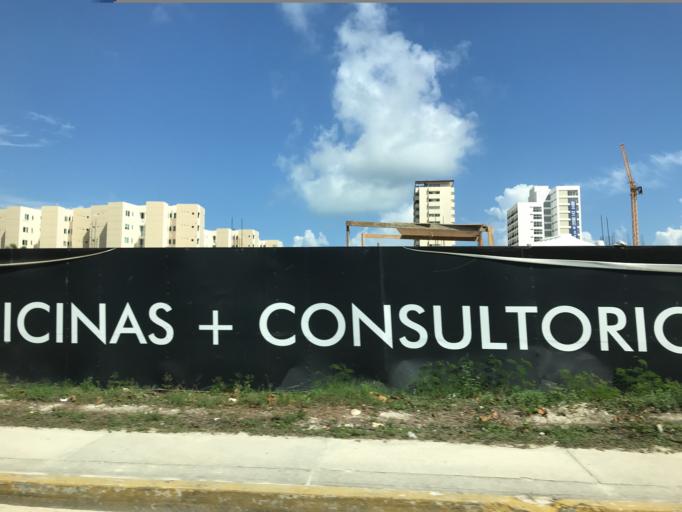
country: MX
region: Quintana Roo
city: Cancun
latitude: 21.1517
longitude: -86.8215
